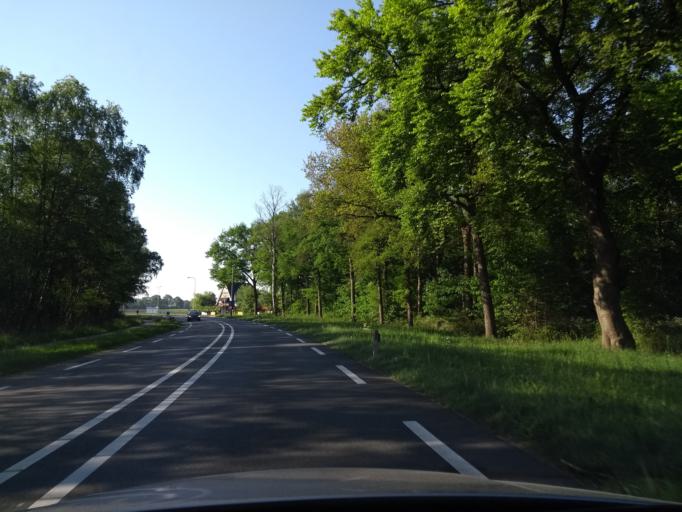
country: NL
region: Overijssel
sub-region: Gemeente Haaksbergen
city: Haaksbergen
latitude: 52.2027
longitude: 6.7298
